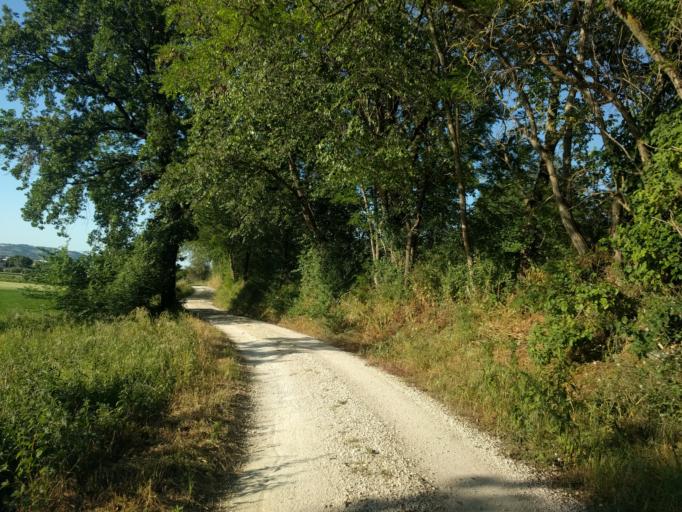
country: IT
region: The Marches
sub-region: Provincia di Pesaro e Urbino
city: Montemaggiore al Metauro
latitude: 43.7439
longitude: 12.9523
